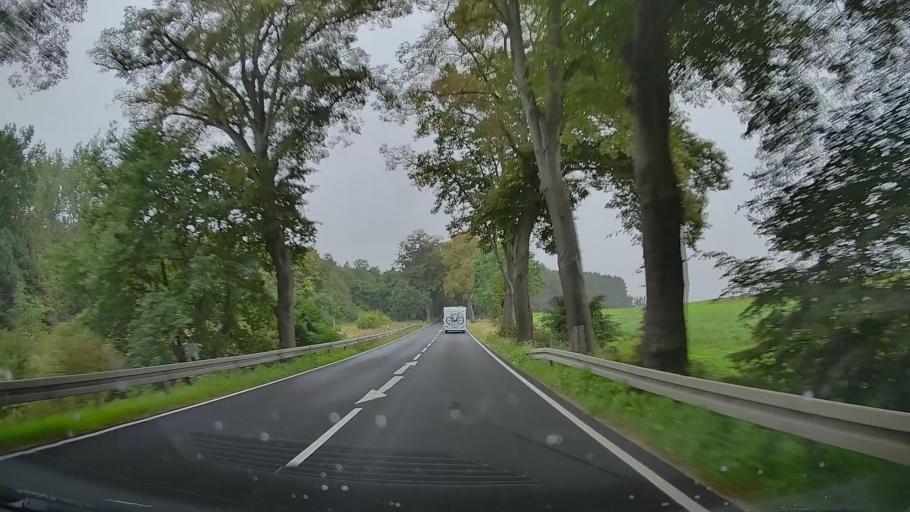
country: DE
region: Mecklenburg-Vorpommern
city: Gaegelow
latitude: 53.7200
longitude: 11.9132
